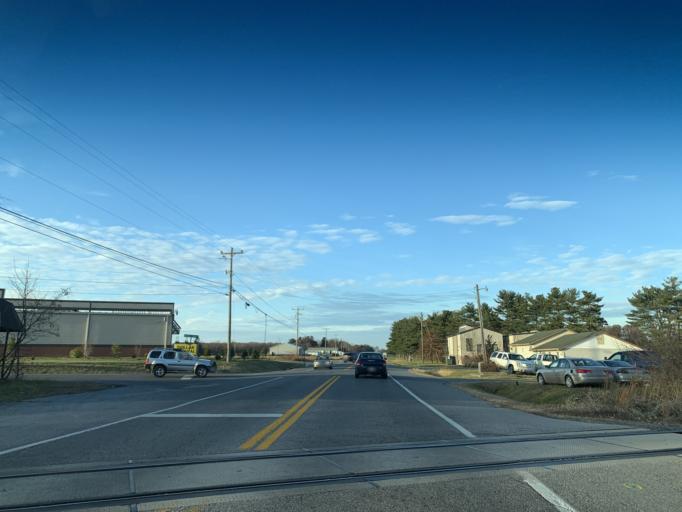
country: US
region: Maryland
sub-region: Kent County
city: Chestertown
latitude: 39.2747
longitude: -76.0921
